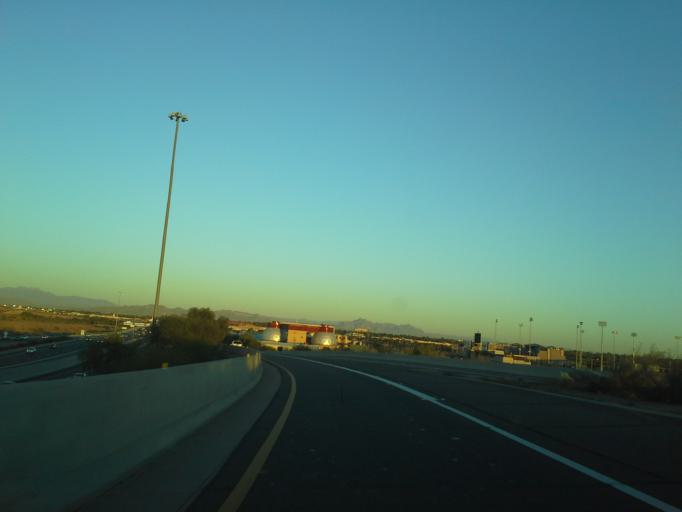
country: US
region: Arizona
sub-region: Maricopa County
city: Tempe
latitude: 33.4330
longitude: -111.8878
